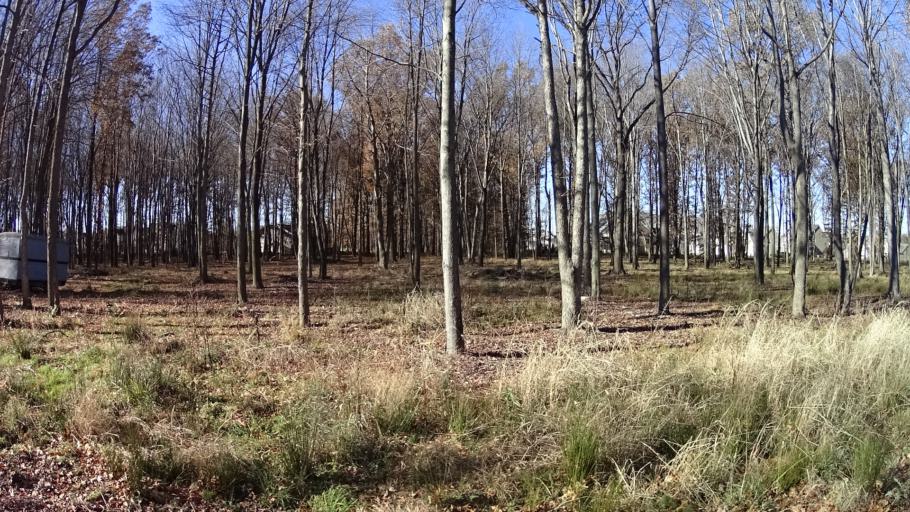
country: US
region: Ohio
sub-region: Lorain County
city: Avon Center
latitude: 41.4821
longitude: -82.0130
